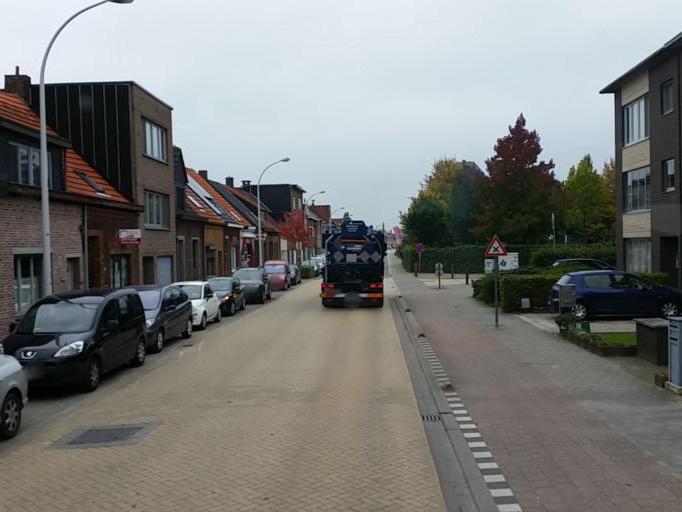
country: BE
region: Flanders
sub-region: Provincie Antwerpen
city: Schoten
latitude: 51.2445
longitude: 4.4708
